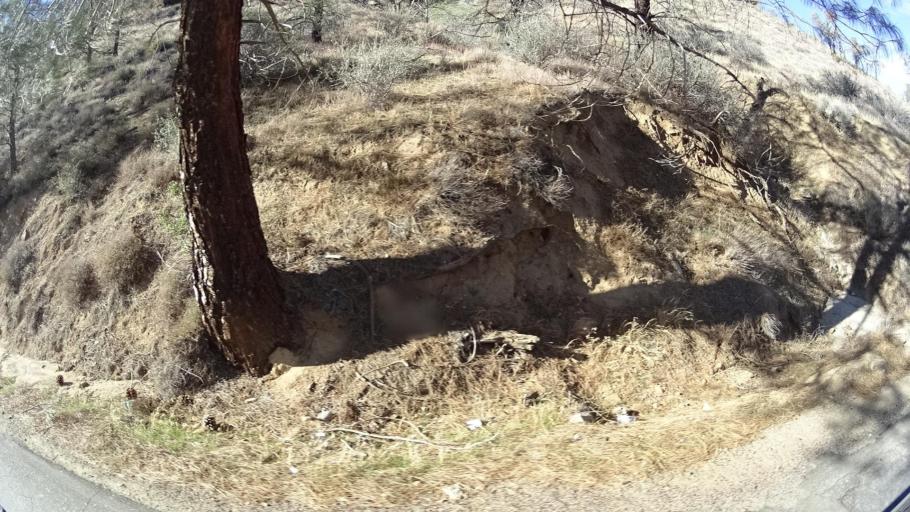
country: US
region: California
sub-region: Kern County
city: Bodfish
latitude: 35.5780
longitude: -118.5034
